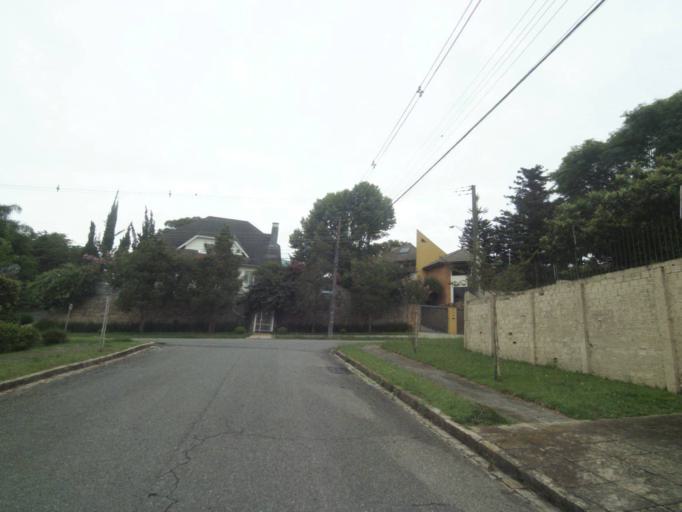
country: BR
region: Parana
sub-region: Curitiba
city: Curitiba
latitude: -25.4060
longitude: -49.2894
